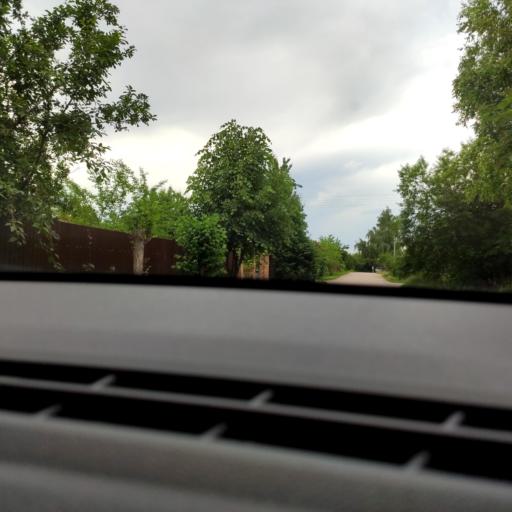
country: RU
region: Samara
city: Podstepki
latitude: 53.5120
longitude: 49.0759
